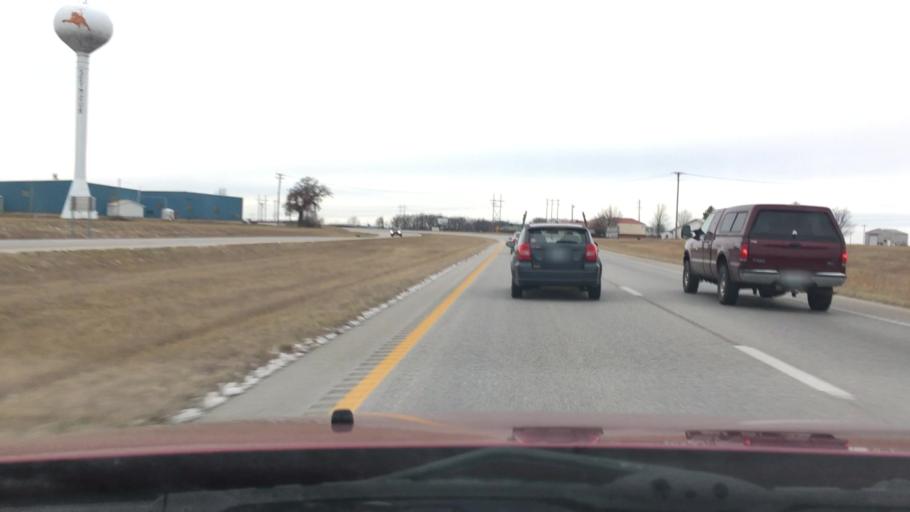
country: US
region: Missouri
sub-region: Webster County
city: Seymour
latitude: 37.1527
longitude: -92.7562
